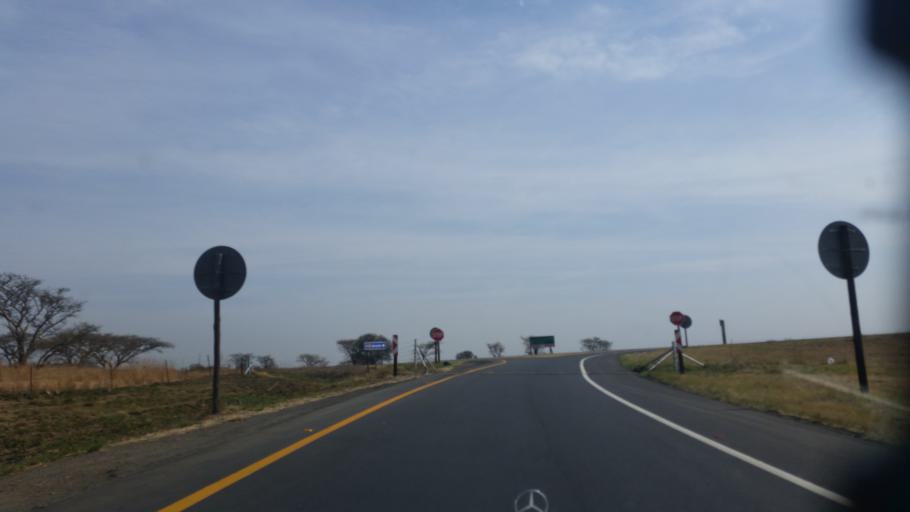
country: ZA
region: KwaZulu-Natal
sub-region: uThukela District Municipality
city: Estcourt
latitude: -28.8816
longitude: 29.7427
